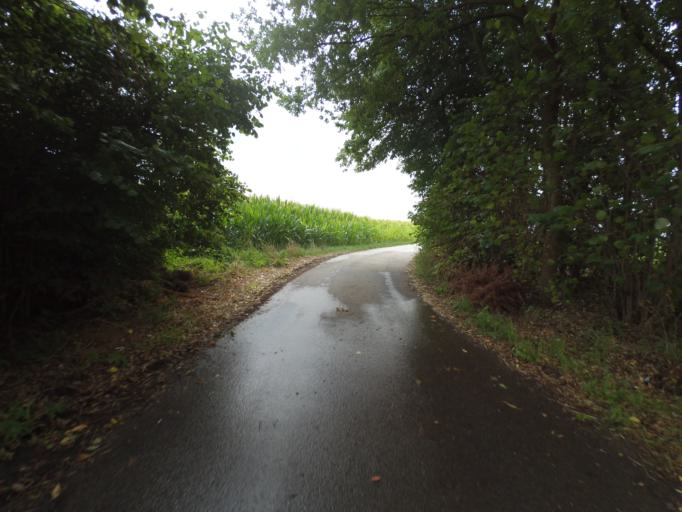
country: DE
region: North Rhine-Westphalia
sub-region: Regierungsbezirk Koln
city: Heinsberg
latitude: 51.0534
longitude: 6.0562
